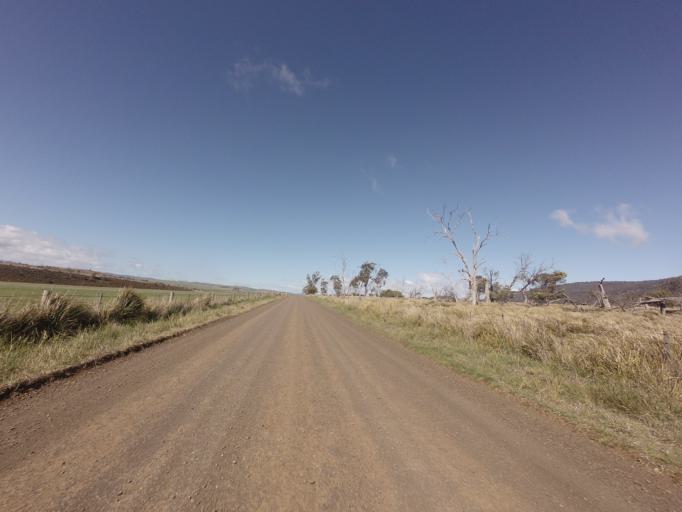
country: AU
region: Tasmania
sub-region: Northern Midlands
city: Evandale
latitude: -41.9454
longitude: 147.4304
